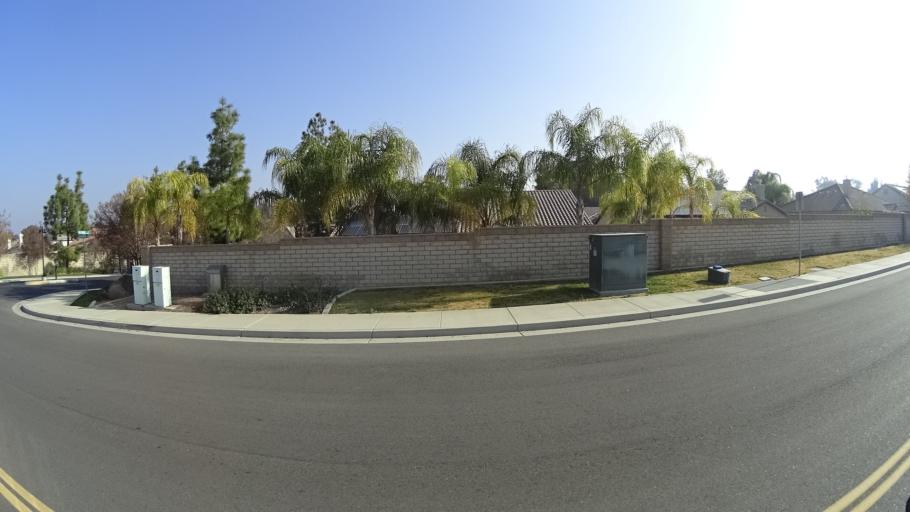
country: US
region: California
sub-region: Kern County
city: Lamont
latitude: 35.4009
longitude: -118.8454
